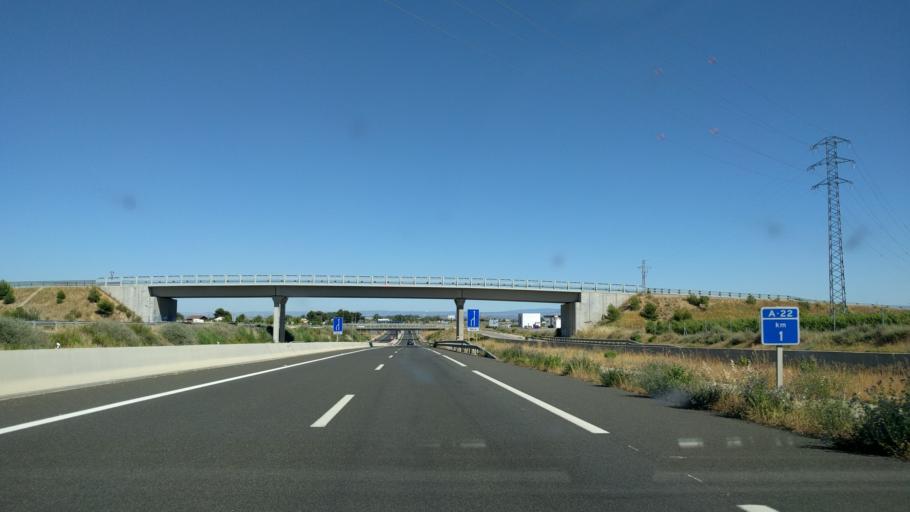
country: ES
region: Catalonia
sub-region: Provincia de Lleida
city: Alpicat
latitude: 41.6503
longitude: 0.5556
